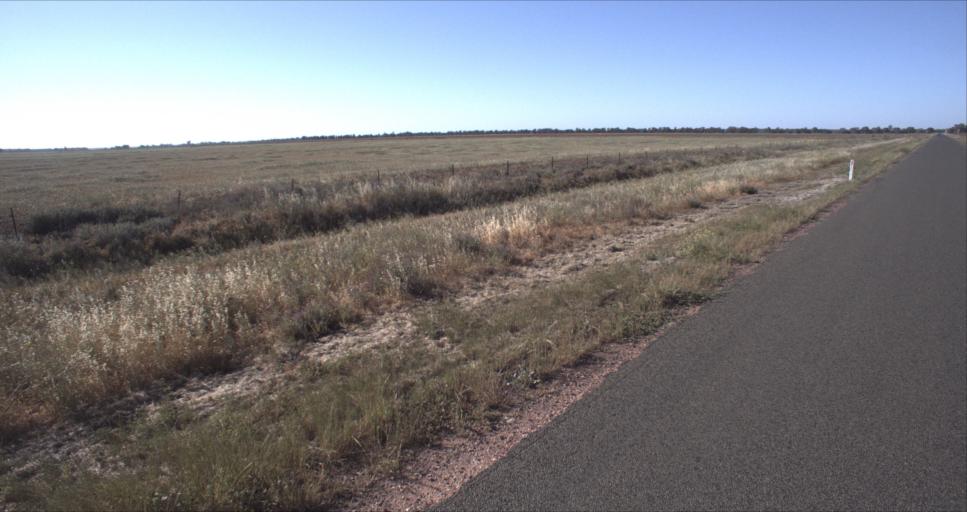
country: AU
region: New South Wales
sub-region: Leeton
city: Leeton
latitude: -34.5645
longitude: 146.2647
